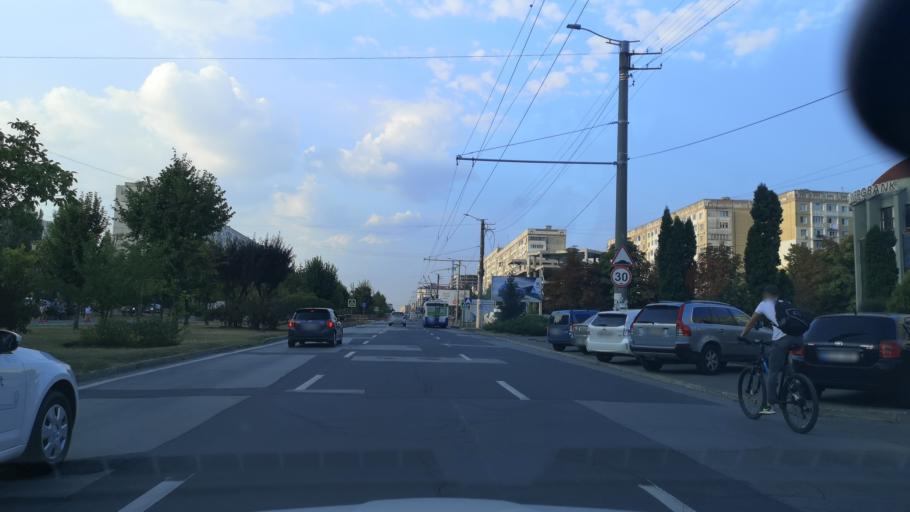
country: MD
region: Chisinau
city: Chisinau
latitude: 47.0392
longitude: 28.8901
